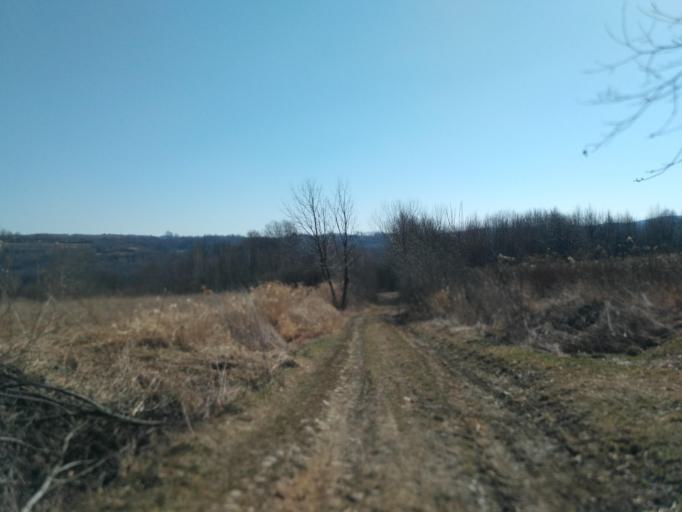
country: PL
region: Subcarpathian Voivodeship
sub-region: Powiat brzozowski
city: Domaradz
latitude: 49.7958
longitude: 21.9752
